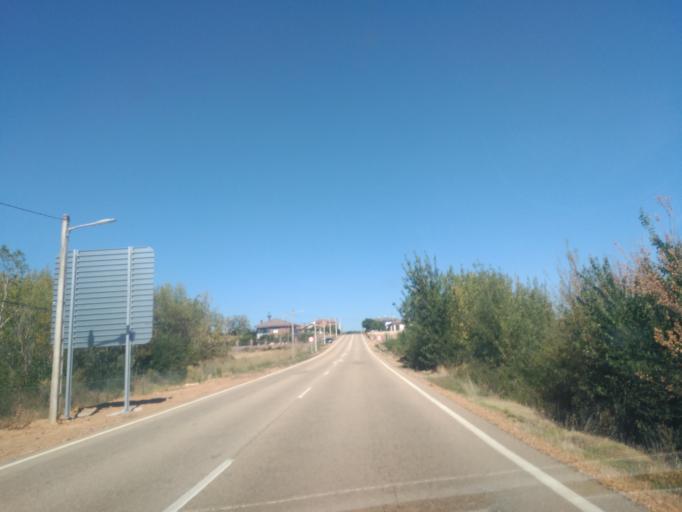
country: ES
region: Castille and Leon
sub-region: Provincia de Zamora
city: Tabara
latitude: 41.8305
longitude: -5.9645
